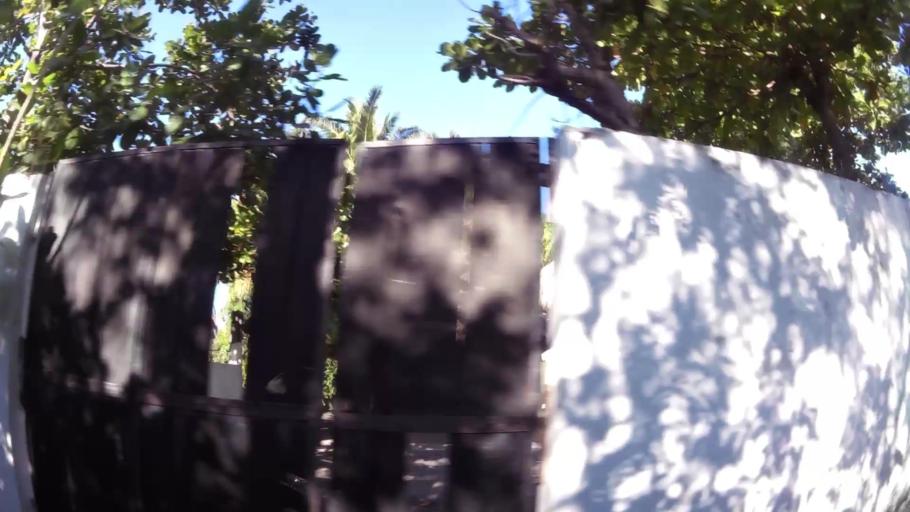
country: GT
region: Santa Rosa
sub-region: Municipio de Taxisco
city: Taxisco
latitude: 13.8936
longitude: -90.4907
